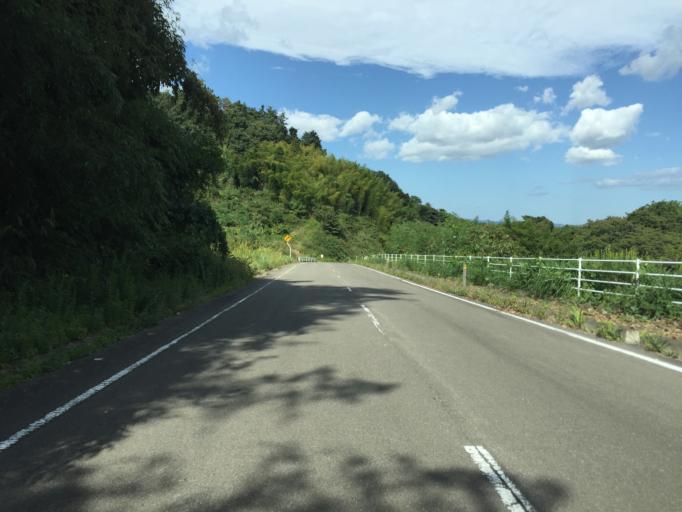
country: JP
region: Fukushima
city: Hobaramachi
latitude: 37.7765
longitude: 140.5376
